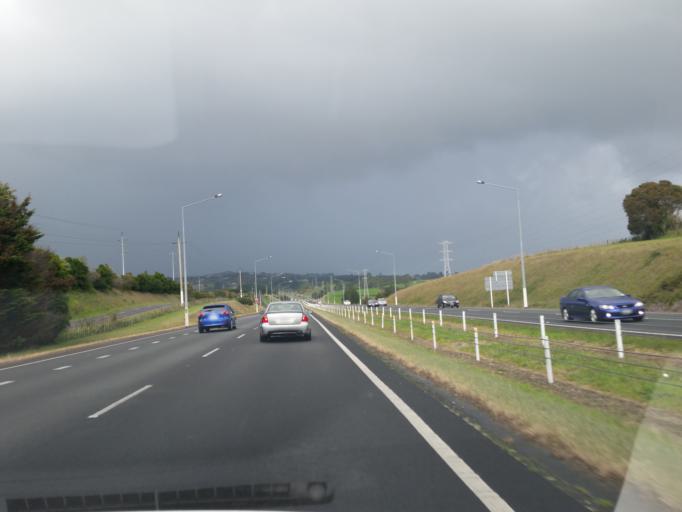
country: NZ
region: Auckland
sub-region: Auckland
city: Pukekohe East
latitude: -37.1469
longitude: 174.9718
